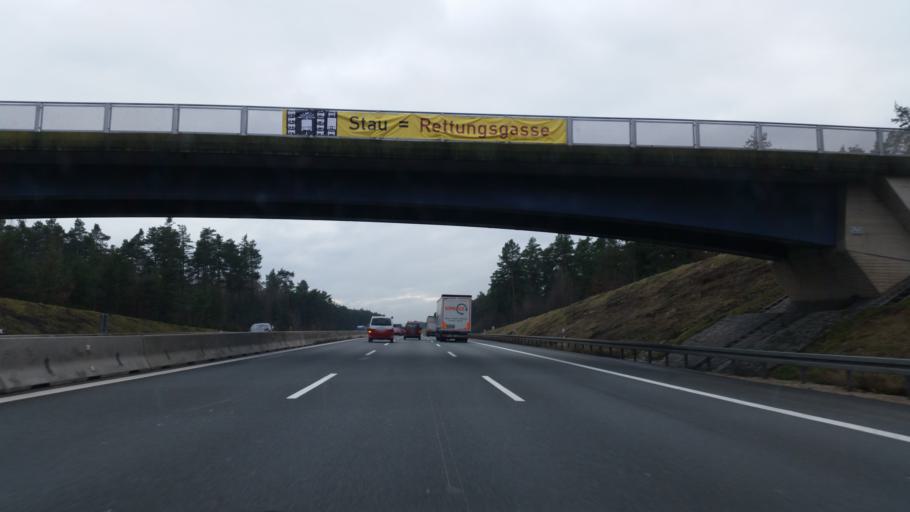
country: DE
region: Bavaria
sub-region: Regierungsbezirk Mittelfranken
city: Wendelstein
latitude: 49.3686
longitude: 11.1240
